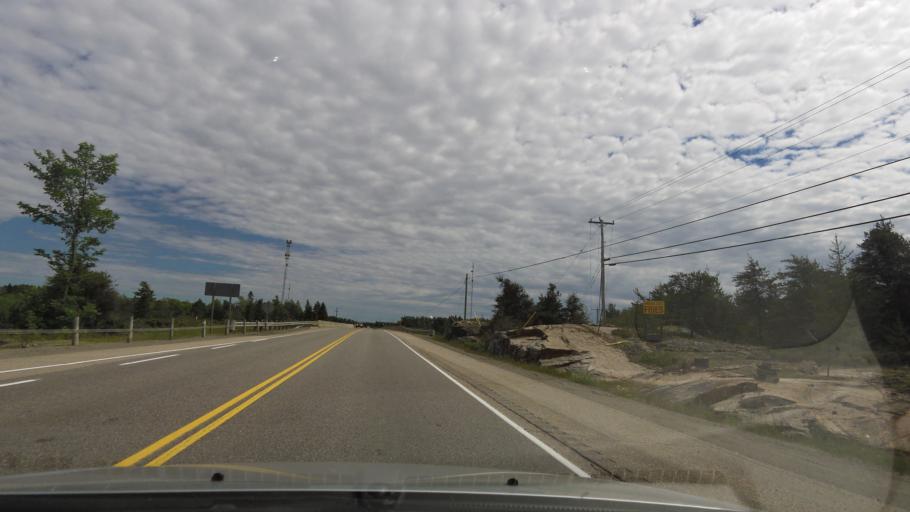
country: CA
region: Ontario
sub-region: Parry Sound District
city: Parry Sound
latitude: 45.8019
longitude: -80.5370
